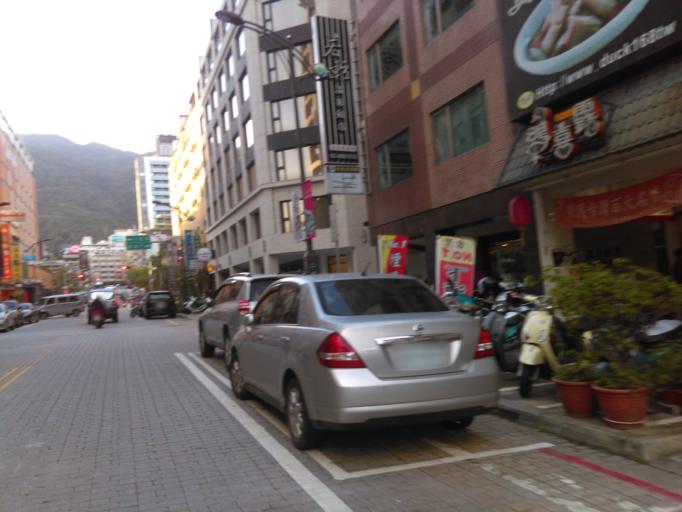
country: TW
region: Taiwan
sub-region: Yilan
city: Yilan
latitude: 24.8278
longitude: 121.7743
